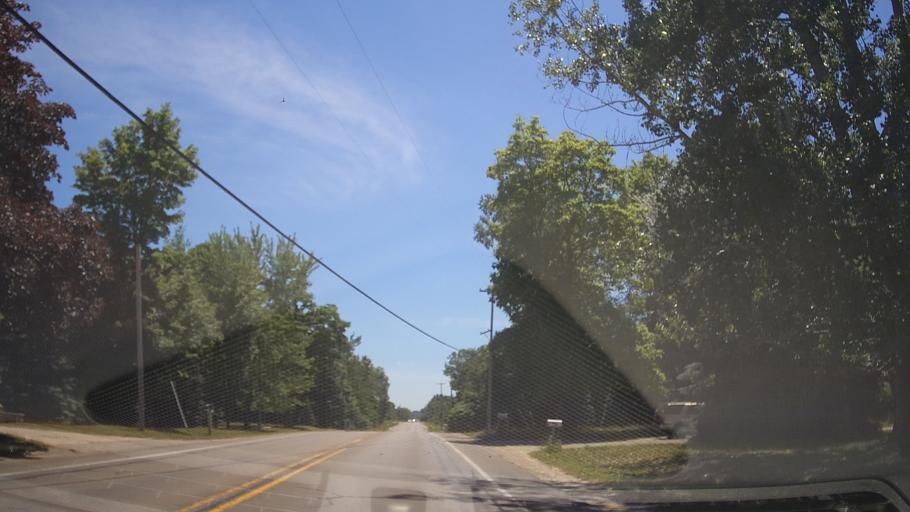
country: US
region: Michigan
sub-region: Grand Traverse County
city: Traverse City
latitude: 44.6857
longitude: -85.6895
